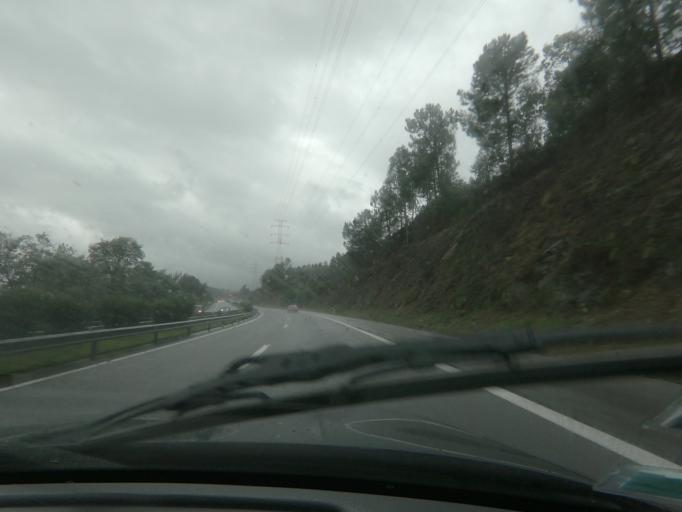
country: PT
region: Porto
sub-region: Paredes
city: Baltar
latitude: 41.1817
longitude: -8.3765
